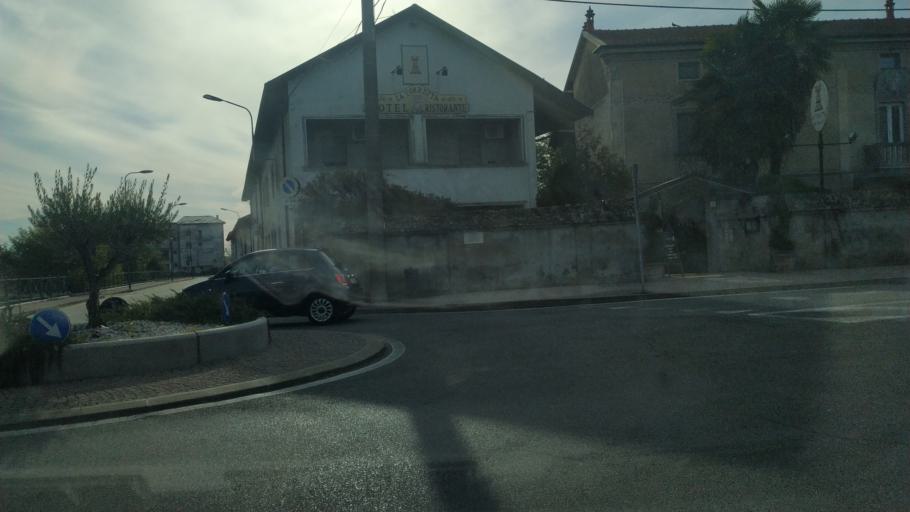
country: IT
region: Piedmont
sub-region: Provincia di Vercelli
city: Bianze
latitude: 45.3059
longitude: 8.1203
